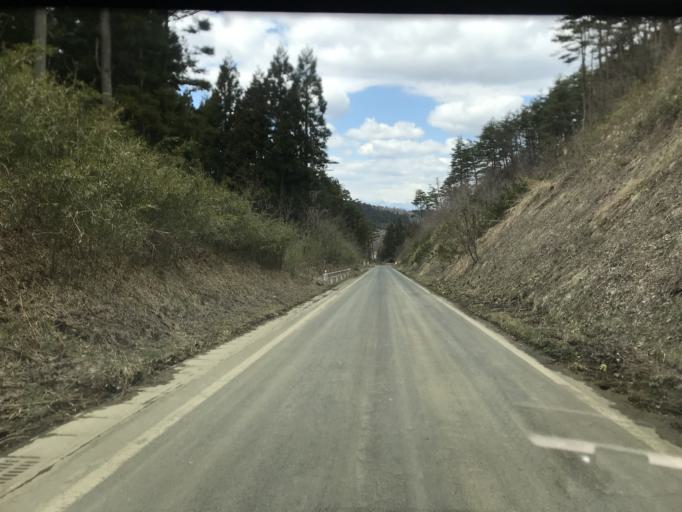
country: JP
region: Iwate
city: Ichinoseki
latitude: 38.9505
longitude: 141.0908
